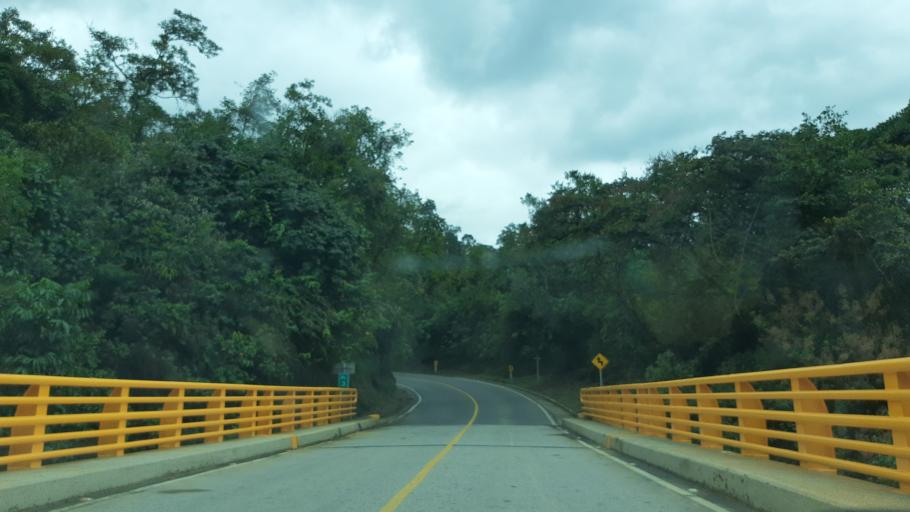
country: CO
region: Boyaca
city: Chivor
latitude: 4.9486
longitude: -73.3044
